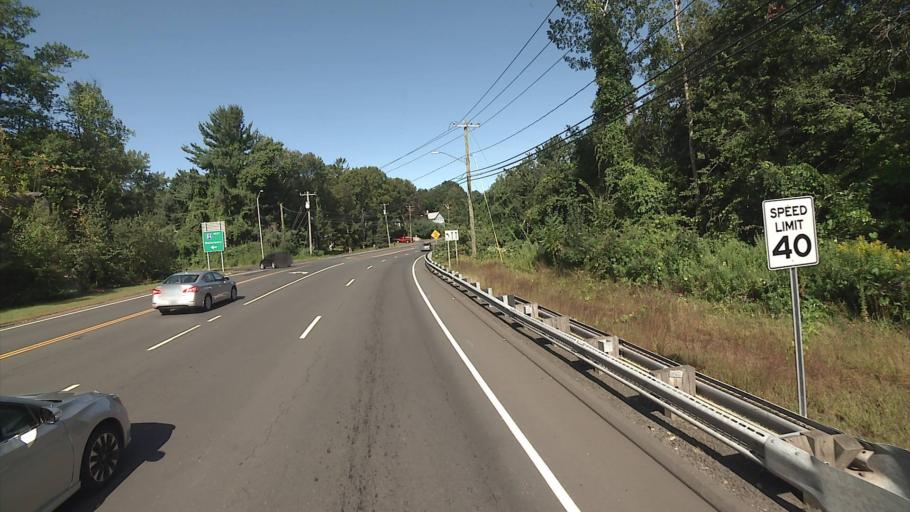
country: US
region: Connecticut
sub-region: New Haven County
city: Prospect
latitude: 41.5427
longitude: -72.9550
